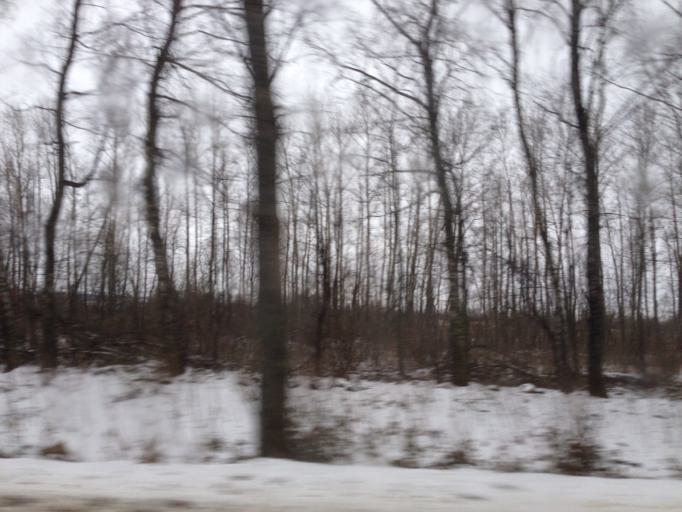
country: RU
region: Tula
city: Partizan
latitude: 54.0037
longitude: 38.1155
